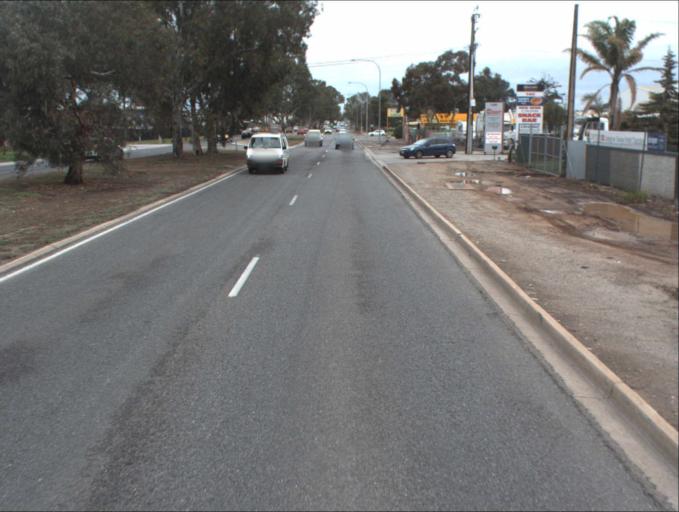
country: AU
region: South Australia
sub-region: Port Adelaide Enfield
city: Enfield
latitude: -34.8392
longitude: 138.5939
